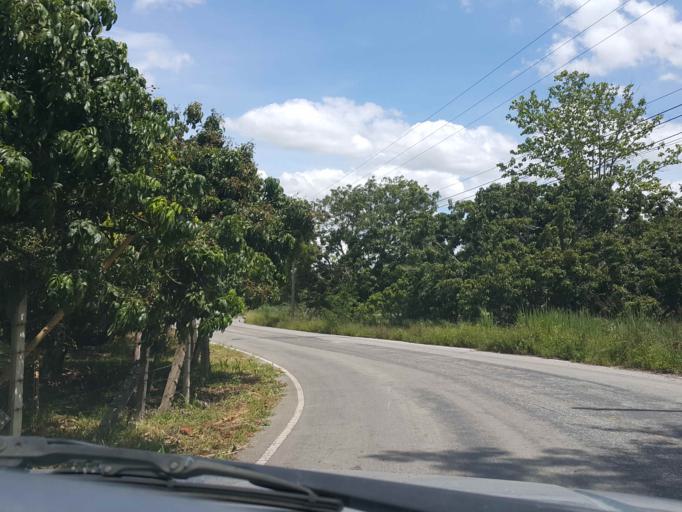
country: TH
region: Chiang Mai
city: Doi Lo
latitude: 18.5300
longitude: 98.7766
